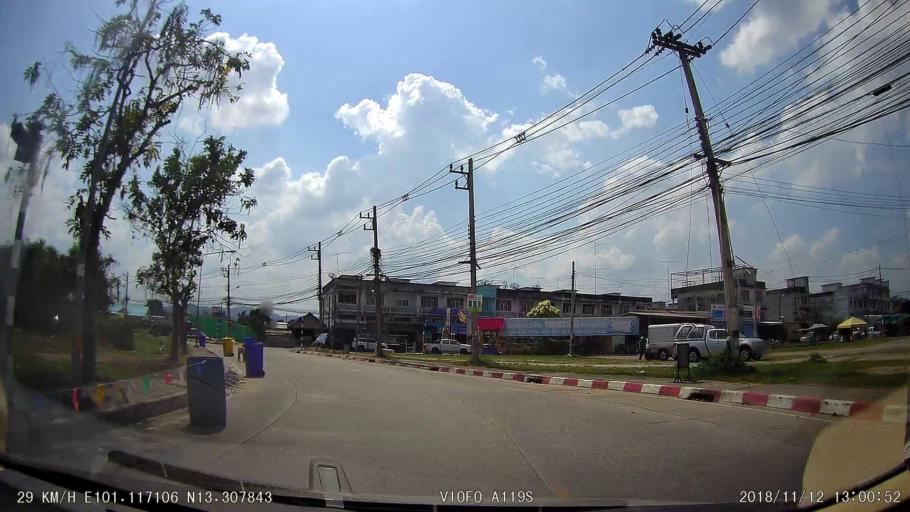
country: TH
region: Chon Buri
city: Ban Bueng
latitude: 13.3078
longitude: 101.1171
